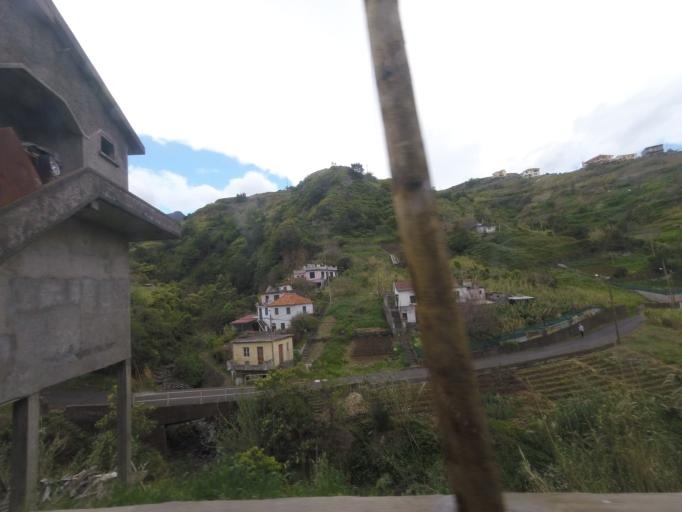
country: PT
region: Madeira
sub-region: Santana
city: Santana
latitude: 32.7624
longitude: -16.8228
